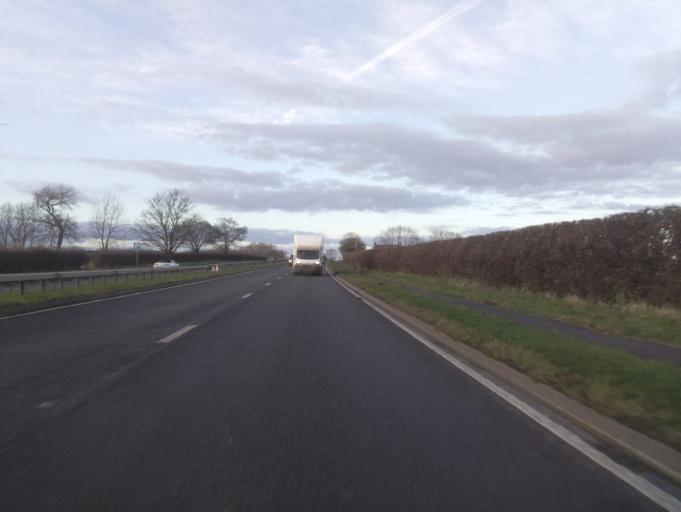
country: GB
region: England
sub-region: Staffordshire
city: Stafford
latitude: 52.8420
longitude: -2.1366
